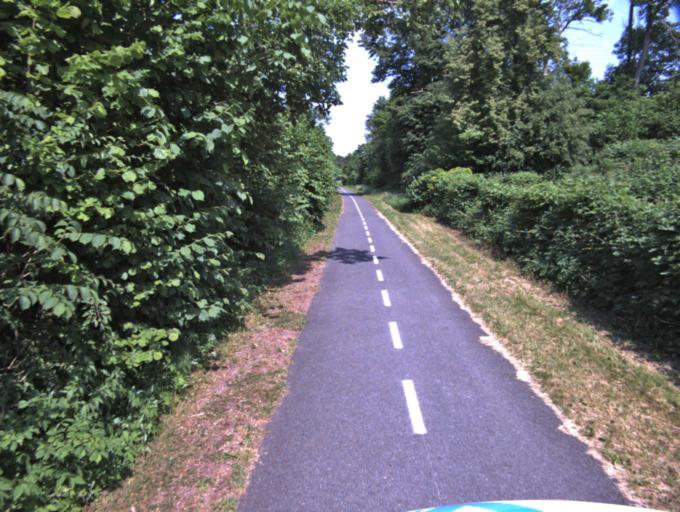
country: SE
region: Skane
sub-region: Kristianstads Kommun
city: Fjalkinge
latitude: 56.0855
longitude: 14.2307
